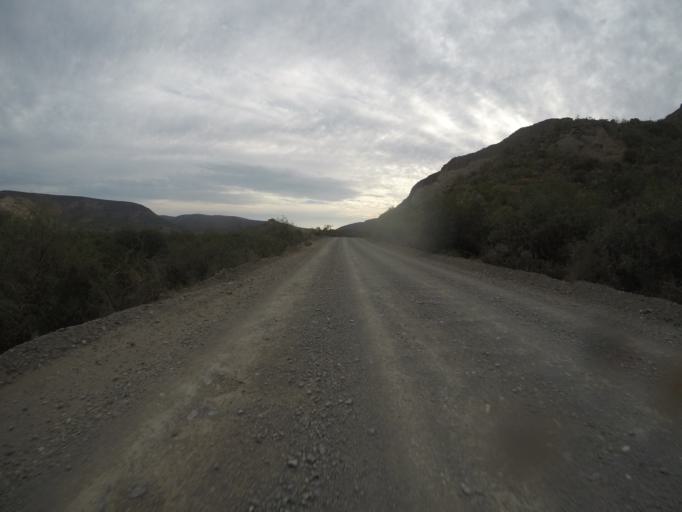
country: ZA
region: Eastern Cape
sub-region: Cacadu District Municipality
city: Willowmore
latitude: -33.5193
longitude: 23.6880
